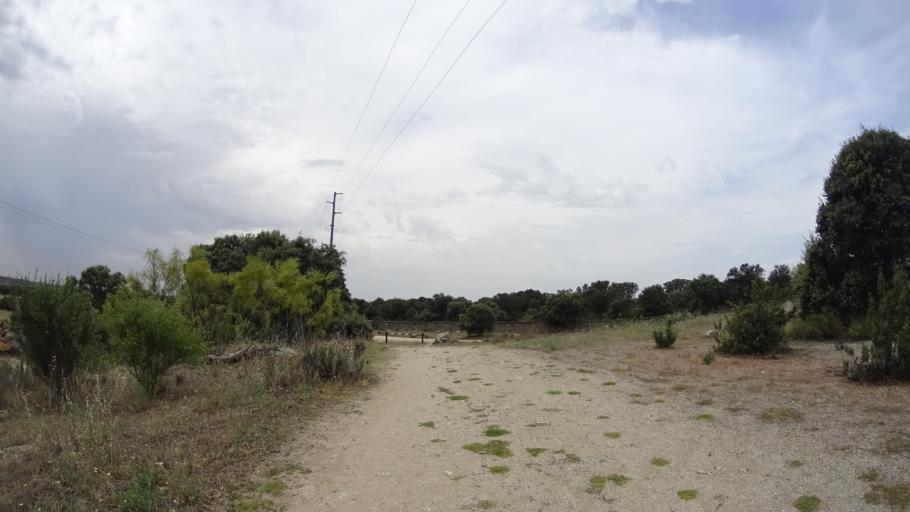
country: ES
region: Madrid
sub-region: Provincia de Madrid
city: Colmenarejo
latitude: 40.5673
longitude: -4.0336
